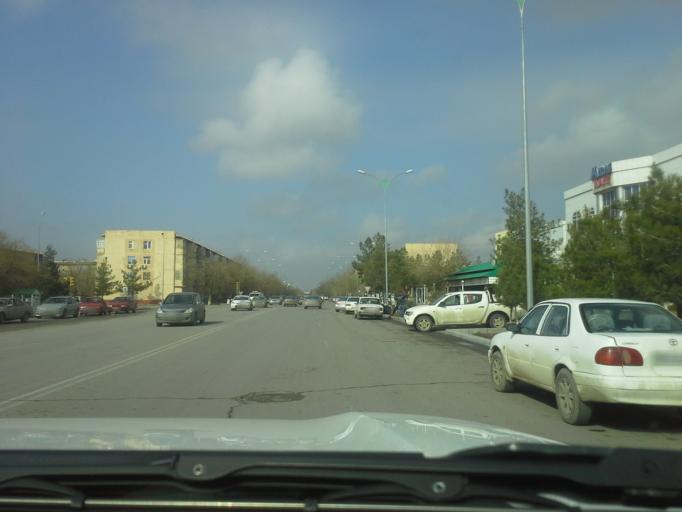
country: TM
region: Mary
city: Mary
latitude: 37.5920
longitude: 61.8350
